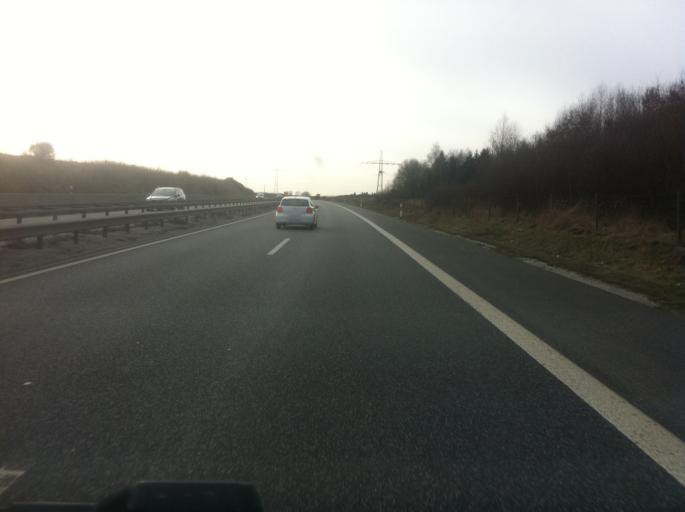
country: DE
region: Rheinland-Pfalz
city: Heinzenbach
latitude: 49.9578
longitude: 7.4146
